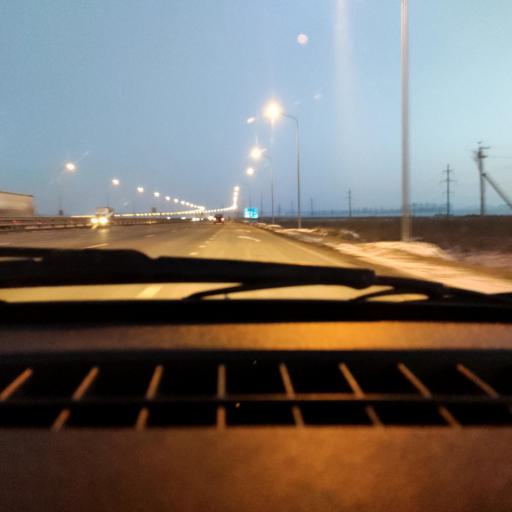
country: RU
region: Bashkortostan
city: Asanovo
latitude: 54.8989
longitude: 55.6335
